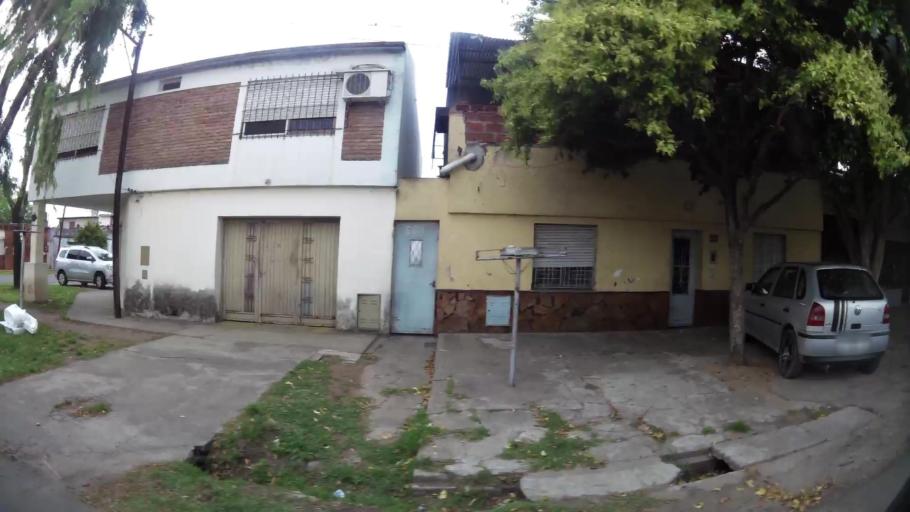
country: AR
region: Santa Fe
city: Gobernador Galvez
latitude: -32.9958
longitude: -60.6680
